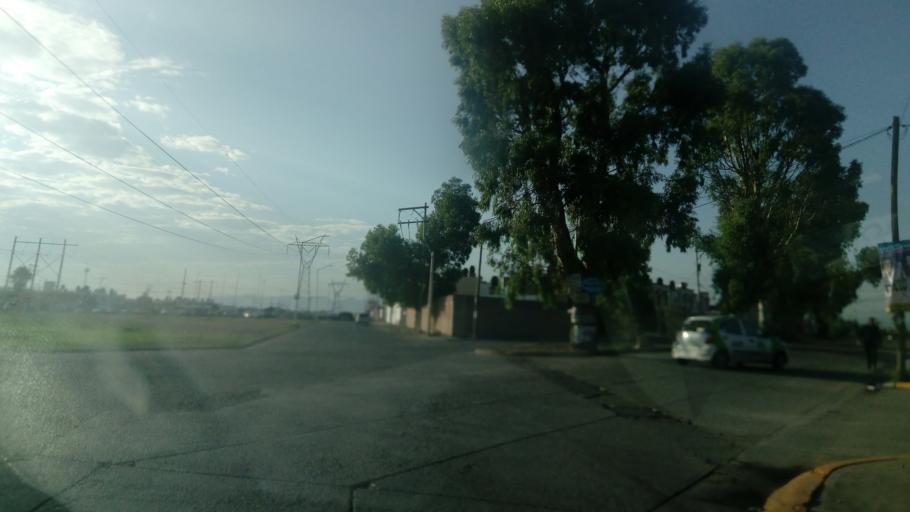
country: MX
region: Durango
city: Victoria de Durango
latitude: 24.0744
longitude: -104.5878
